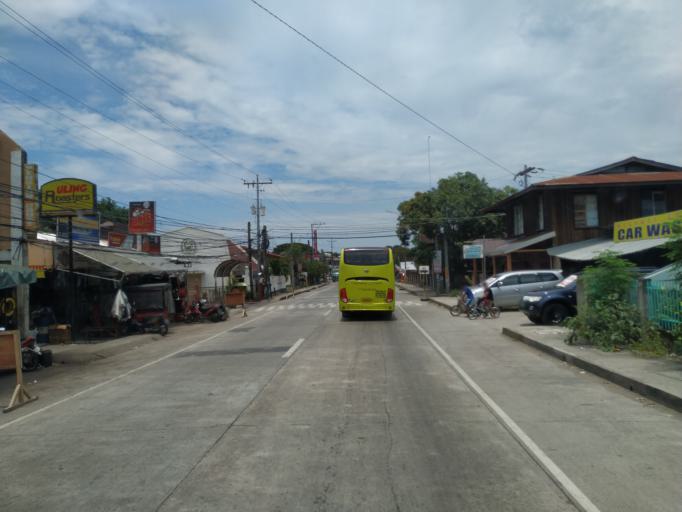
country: PH
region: Central Visayas
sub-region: Province of Negros Oriental
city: Sibulan
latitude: 9.3570
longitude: 123.2848
